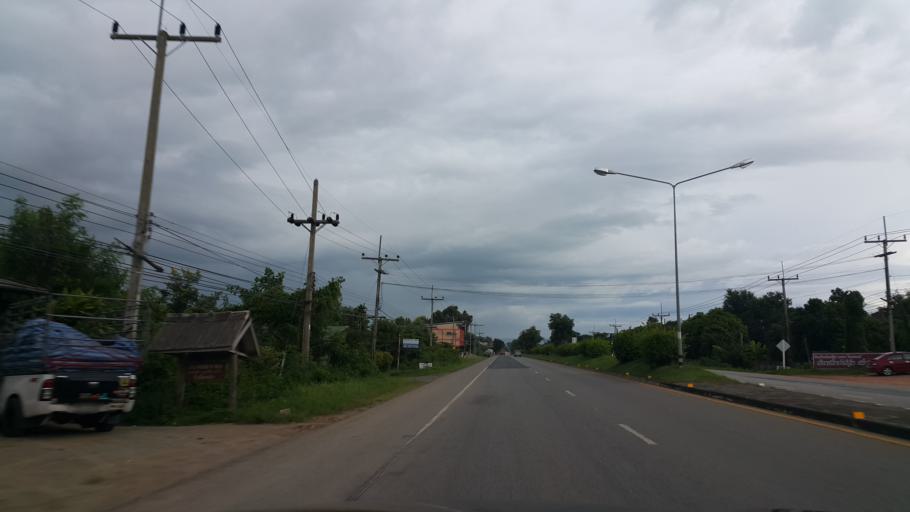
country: TH
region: Phayao
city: Dok Kham Tai
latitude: 19.1466
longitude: 99.9290
